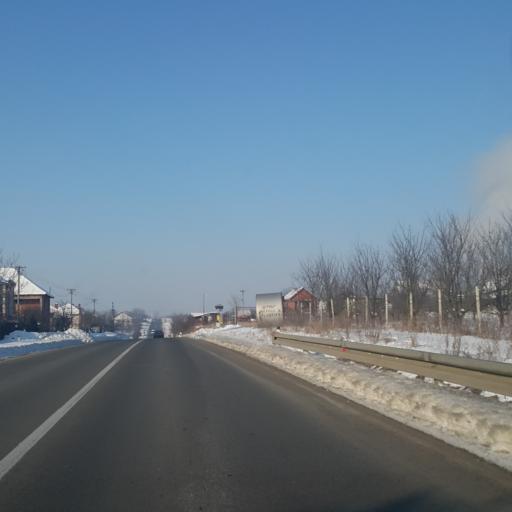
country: RS
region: Central Serbia
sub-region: Toplicki Okrug
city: Prokuplje
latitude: 43.2418
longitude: 21.4780
